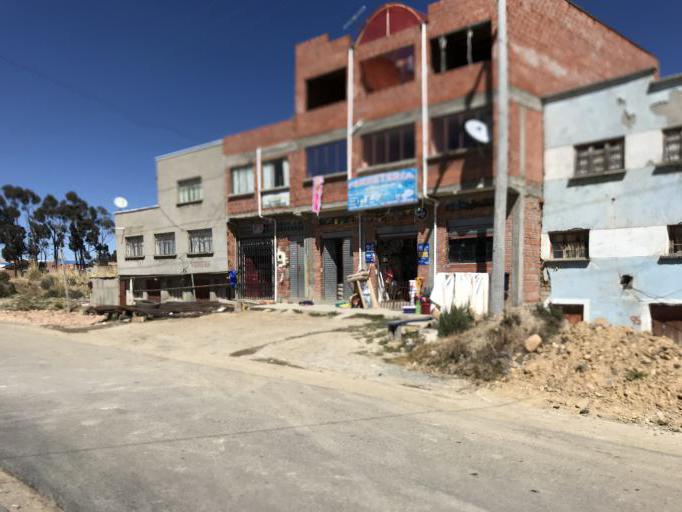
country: BO
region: La Paz
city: Huatajata
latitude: -16.2060
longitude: -68.7038
